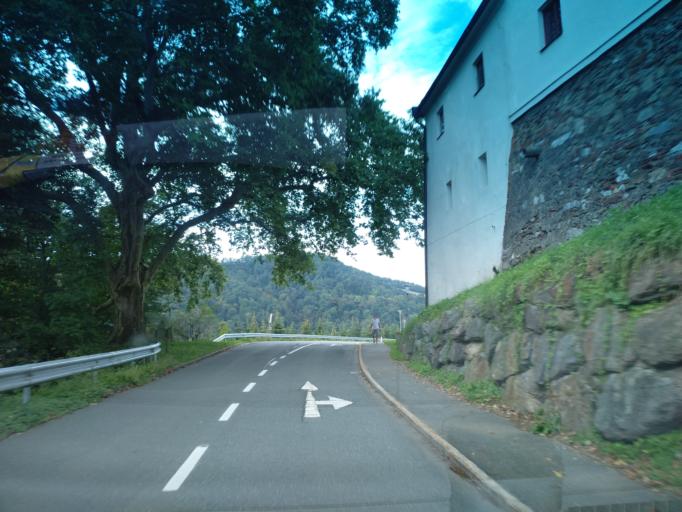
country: AT
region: Styria
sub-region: Politischer Bezirk Leibnitz
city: Leibnitz
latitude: 46.7811
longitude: 15.5232
